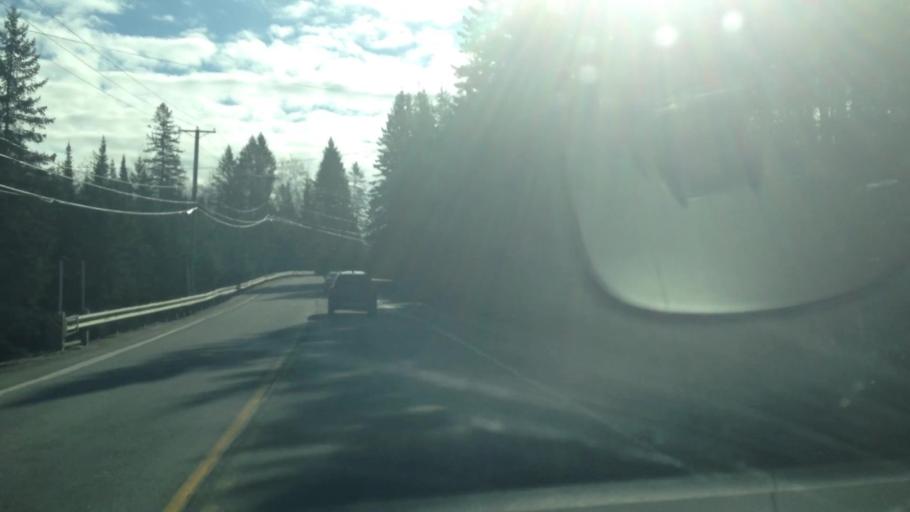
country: CA
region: Quebec
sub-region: Laurentides
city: Sainte-Adele
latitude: 46.0190
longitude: -74.0873
